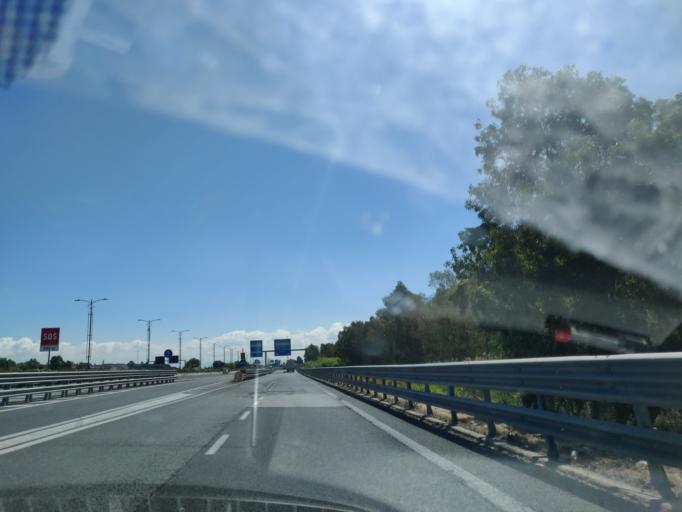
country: IT
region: Latium
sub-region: Citta metropolitana di Roma Capitale
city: Vitinia
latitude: 41.8170
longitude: 12.3793
